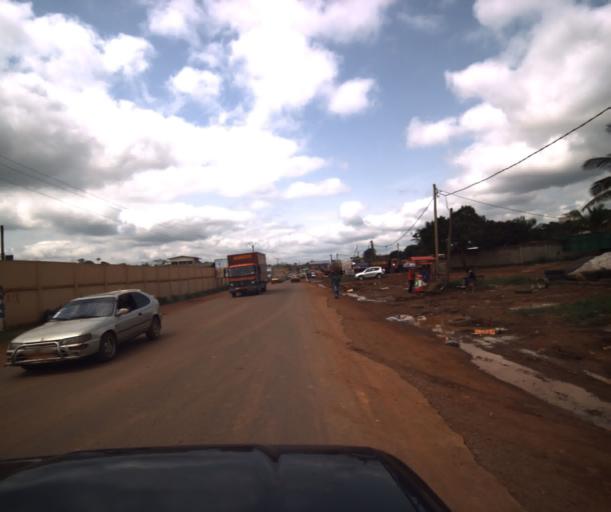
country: CM
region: Centre
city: Yaounde
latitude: 3.8043
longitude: 11.5085
